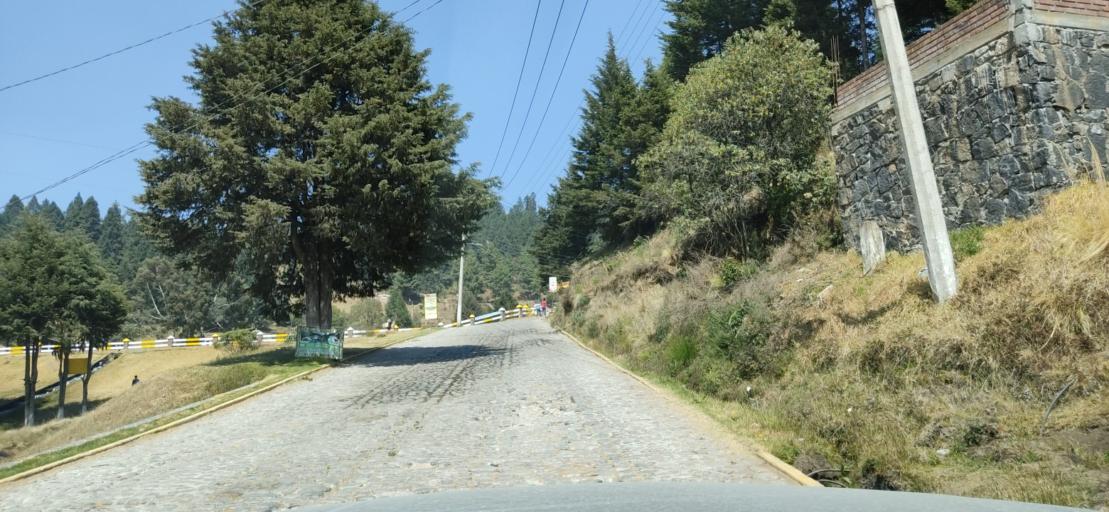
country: MX
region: Mexico
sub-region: Ocoyoacac
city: San Jeronimo Acazulco
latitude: 19.2462
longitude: -99.3772
